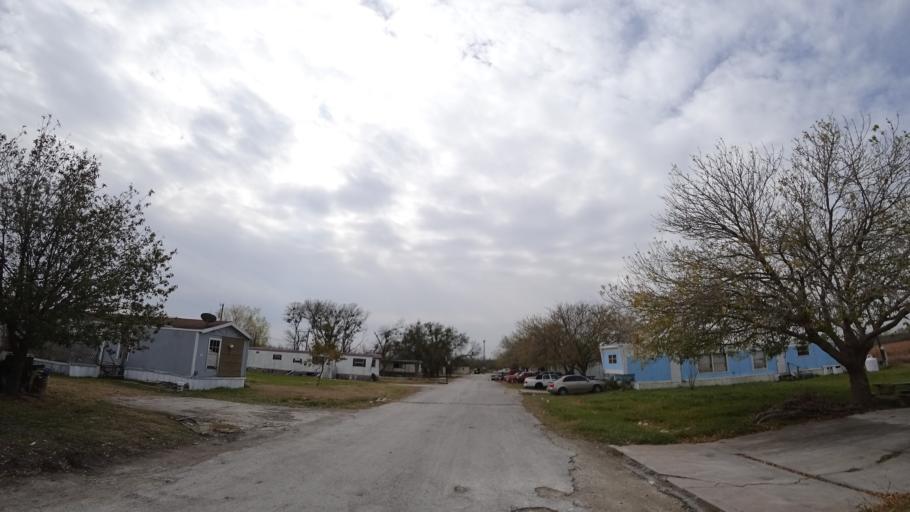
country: US
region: Texas
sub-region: Travis County
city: Garfield
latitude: 30.1441
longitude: -97.6538
